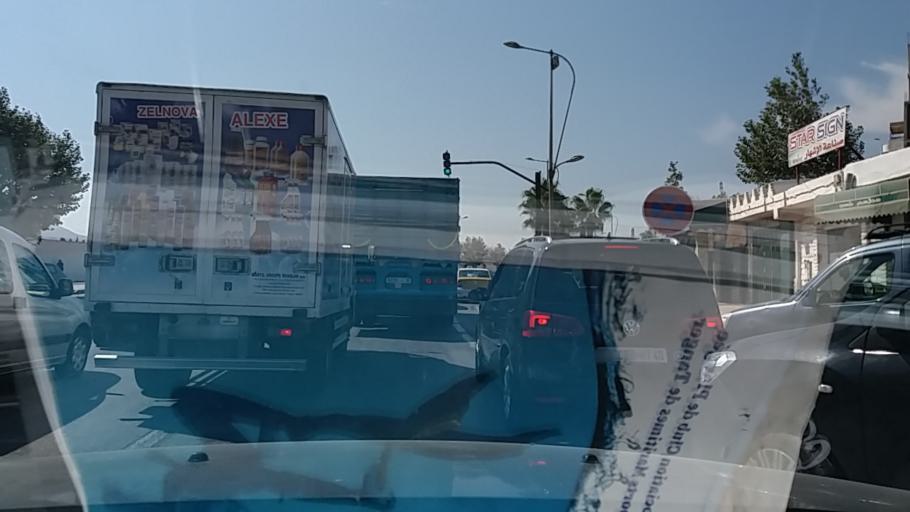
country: MA
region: Tanger-Tetouan
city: Tetouan
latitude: 35.5653
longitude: -5.4003
